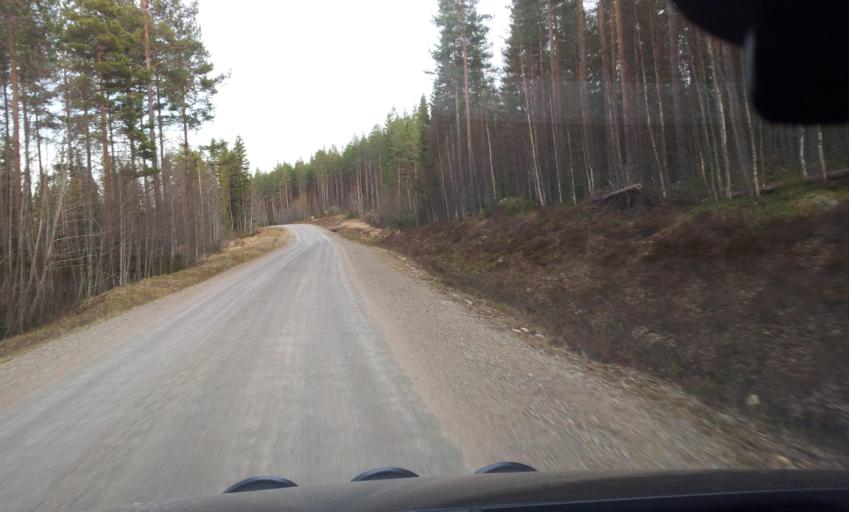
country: SE
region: Gaevleborg
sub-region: Ljusdals Kommun
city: Farila
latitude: 62.1031
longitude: 15.7401
